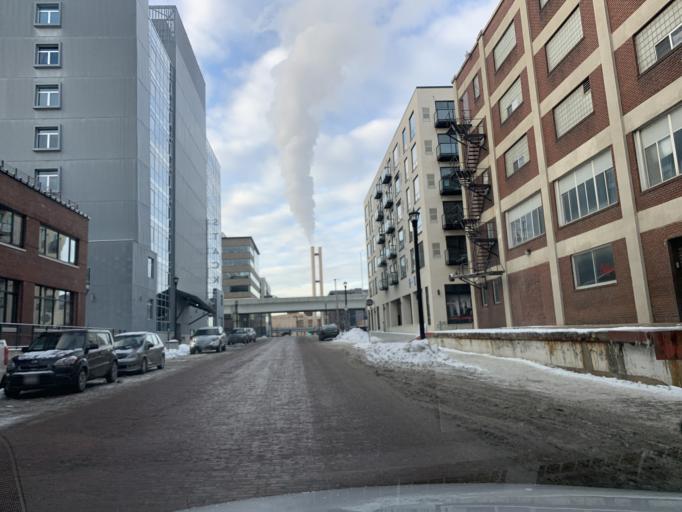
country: US
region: Minnesota
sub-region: Hennepin County
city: Minneapolis
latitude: 44.9859
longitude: -93.2772
